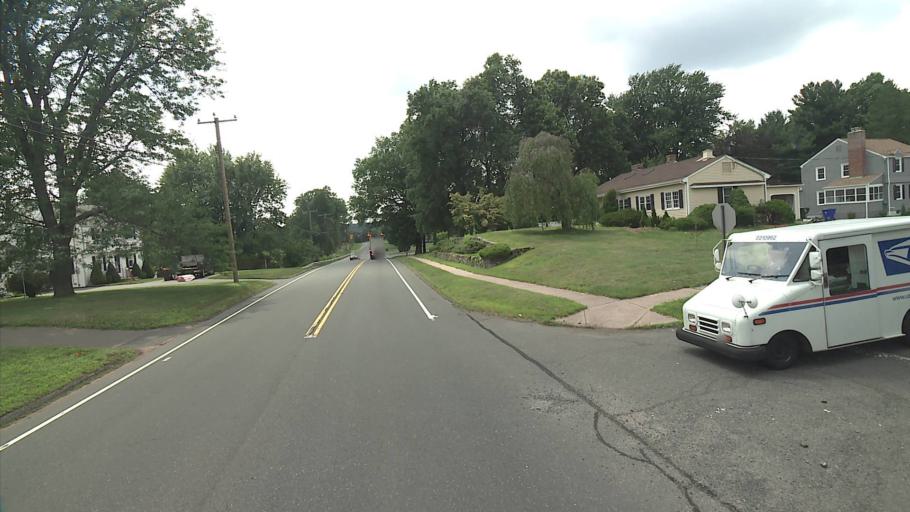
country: US
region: Connecticut
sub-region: Hartford County
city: Wethersfield
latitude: 41.6921
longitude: -72.6790
